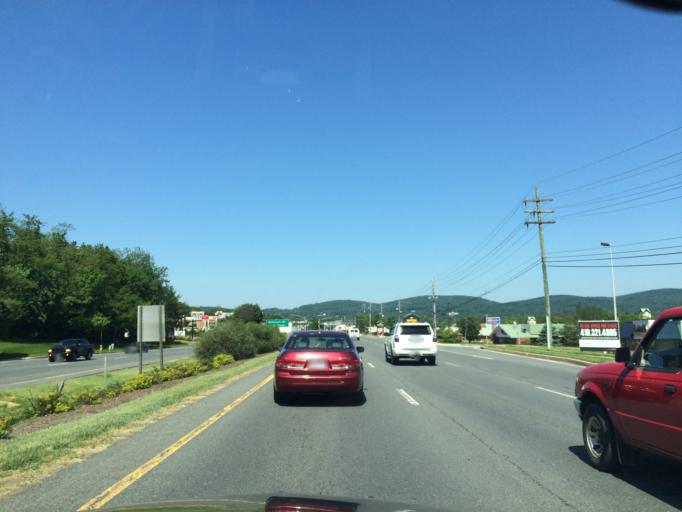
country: US
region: Maryland
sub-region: Frederick County
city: Frederick
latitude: 39.4170
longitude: -77.4422
